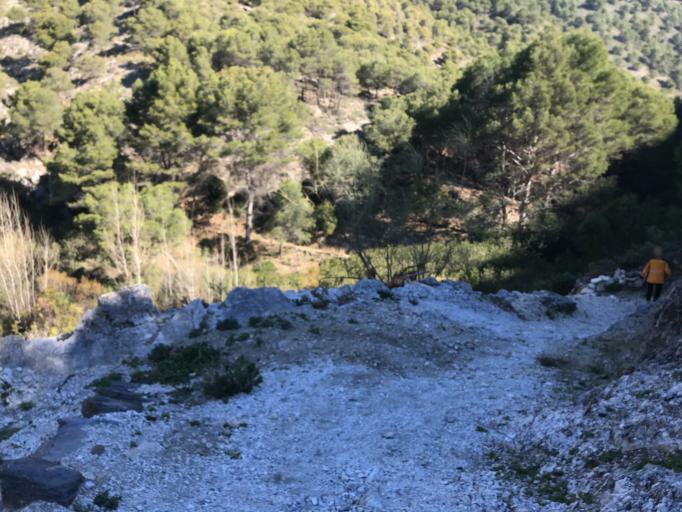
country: ES
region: Andalusia
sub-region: Provincia de Malaga
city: Canillas de Albaida
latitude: 36.8508
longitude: -3.9847
